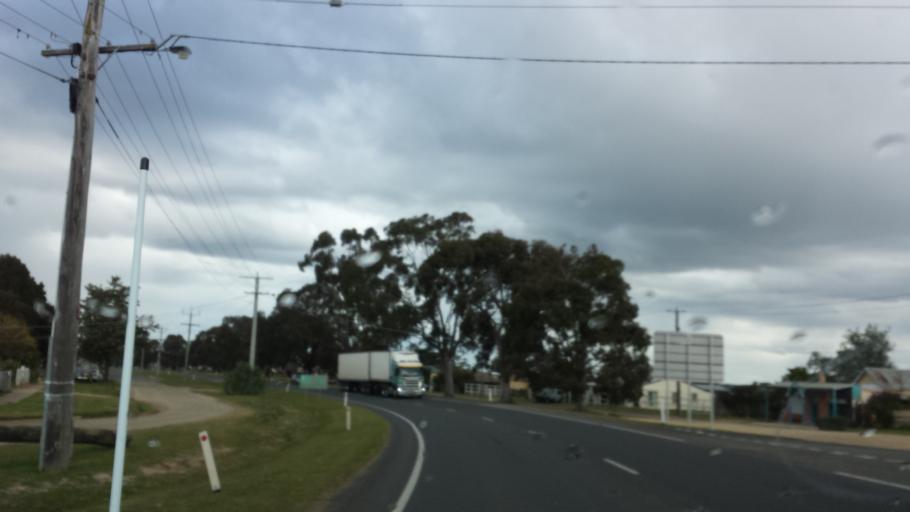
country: AU
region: Victoria
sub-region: East Gippsland
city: Bairnsdale
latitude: -37.8108
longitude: 147.6475
